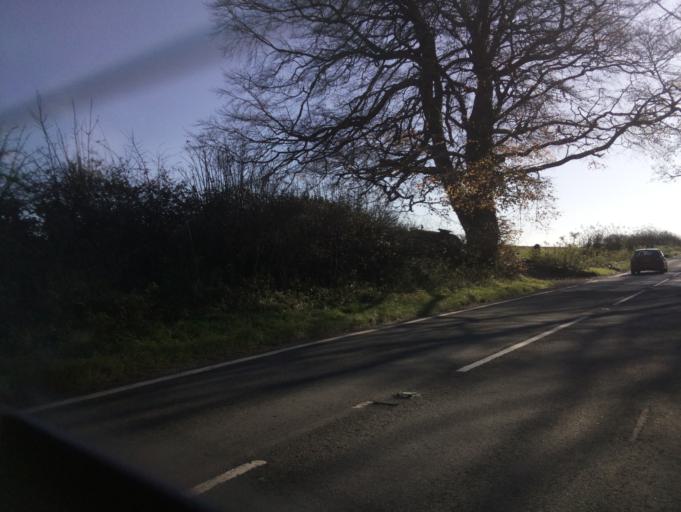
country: GB
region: England
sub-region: Dorset
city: Dorchester
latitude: 50.8313
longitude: -2.4665
